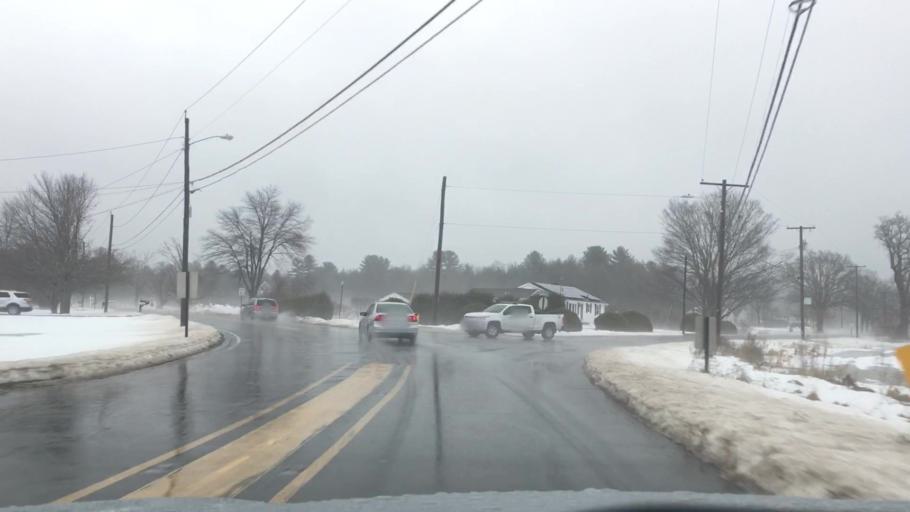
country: US
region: Massachusetts
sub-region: Hampshire County
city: Granby
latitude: 42.2275
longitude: -72.4888
